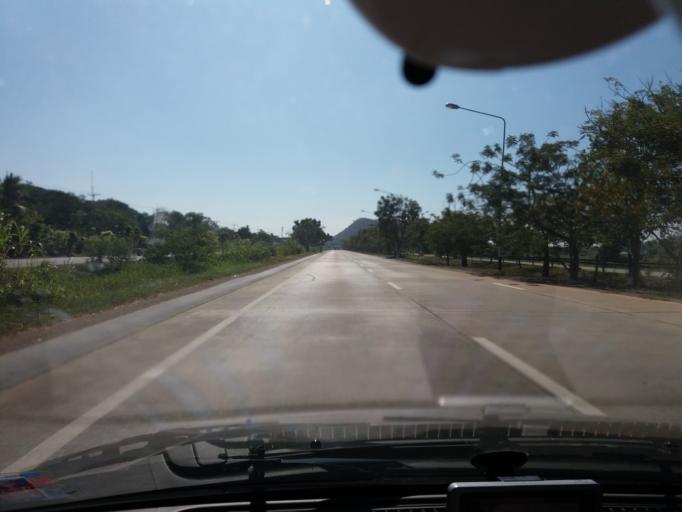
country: TH
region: Suphan Buri
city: Doem Bang Nang Buat
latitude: 14.8560
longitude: 100.0948
